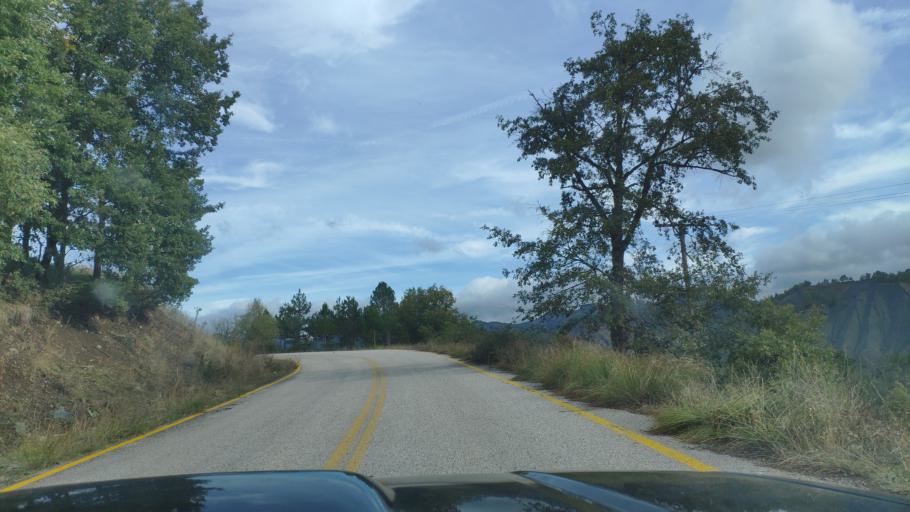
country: GR
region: West Macedonia
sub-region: Nomos Kastorias
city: Nestorio
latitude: 40.2442
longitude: 20.9892
